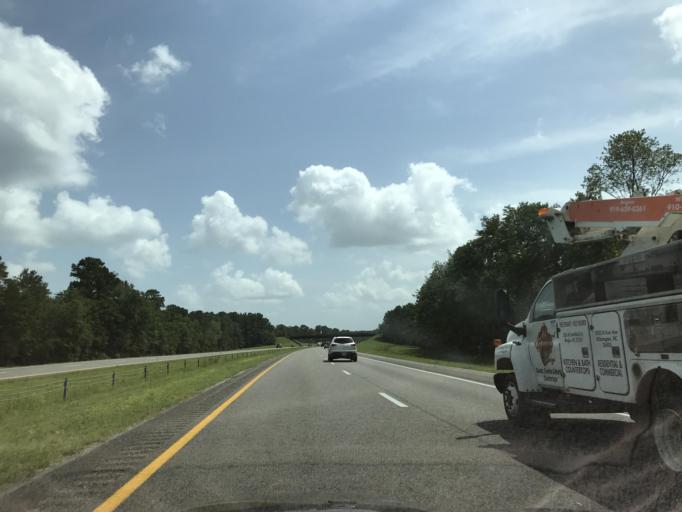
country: US
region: North Carolina
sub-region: Pender County
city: Burgaw
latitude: 34.5076
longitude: -77.8777
